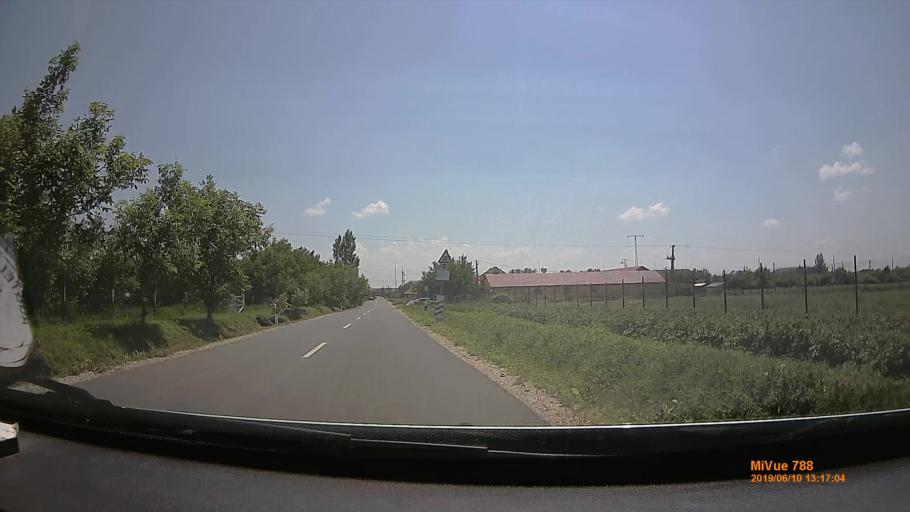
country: HU
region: Borsod-Abauj-Zemplen
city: Tiszaluc
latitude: 48.0411
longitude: 21.0619
